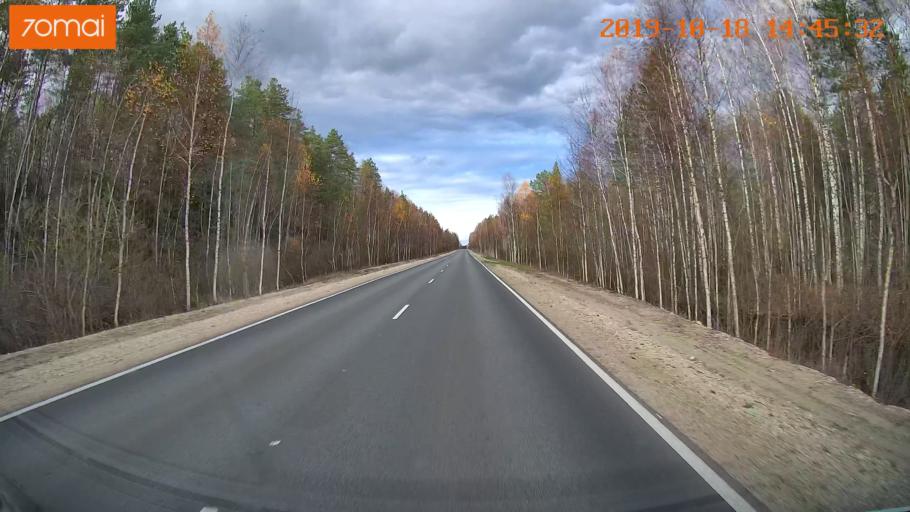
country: RU
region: Vladimir
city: Velikodvorskiy
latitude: 55.3565
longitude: 40.6791
